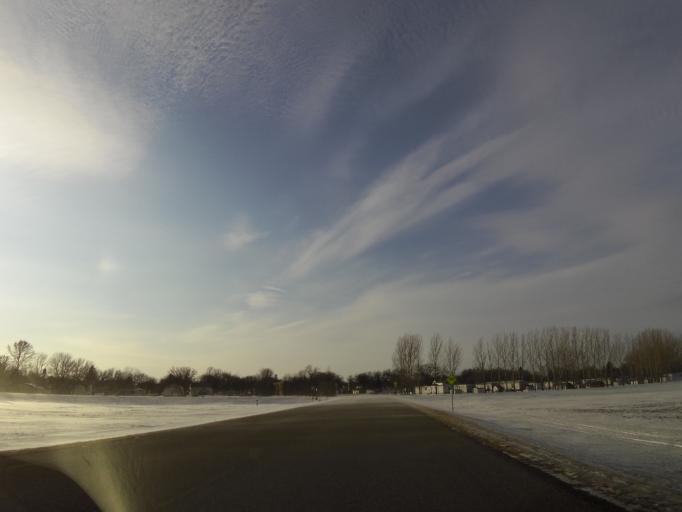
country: US
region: North Dakota
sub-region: Walsh County
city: Grafton
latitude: 48.4183
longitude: -97.3955
